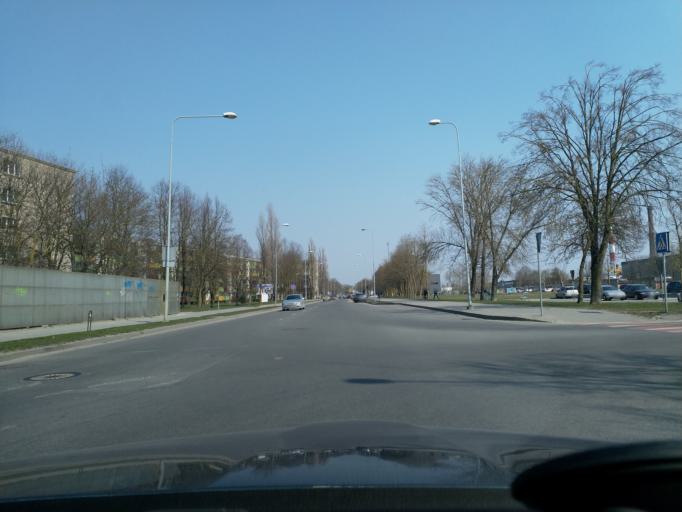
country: LT
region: Klaipedos apskritis
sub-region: Klaipeda
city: Klaipeda
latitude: 55.6955
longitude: 21.1565
